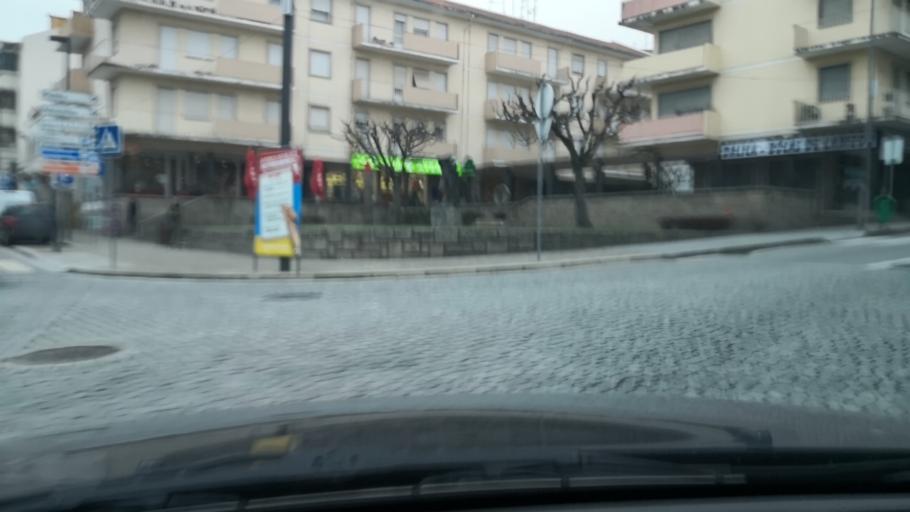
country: PT
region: Viseu
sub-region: Lamego
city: Lamego
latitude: 41.0961
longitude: -7.8087
